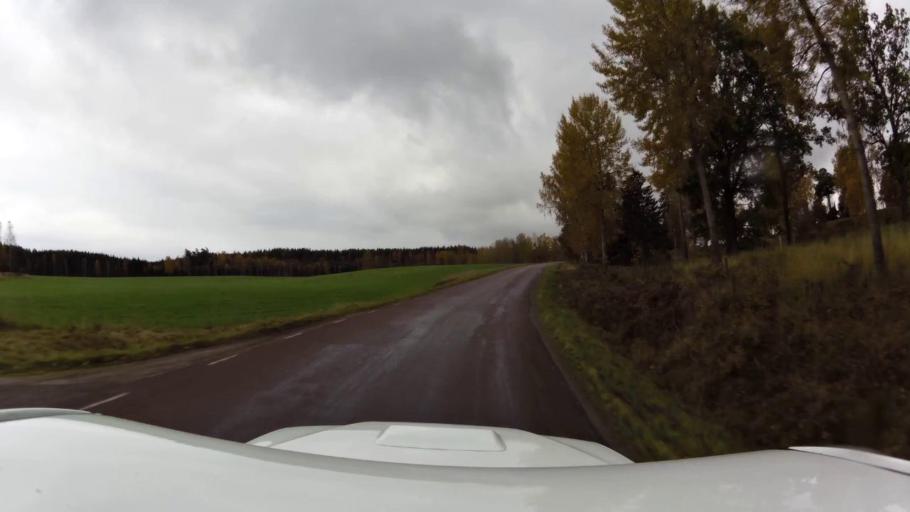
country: SE
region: OEstergoetland
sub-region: Linkopings Kommun
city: Ljungsbro
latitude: 58.5348
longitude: 15.5250
